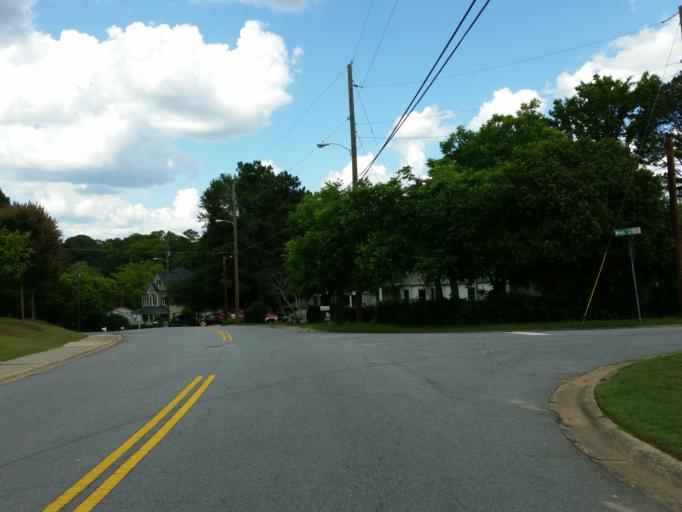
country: US
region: Georgia
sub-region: Cobb County
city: Marietta
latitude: 33.9457
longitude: -84.5309
